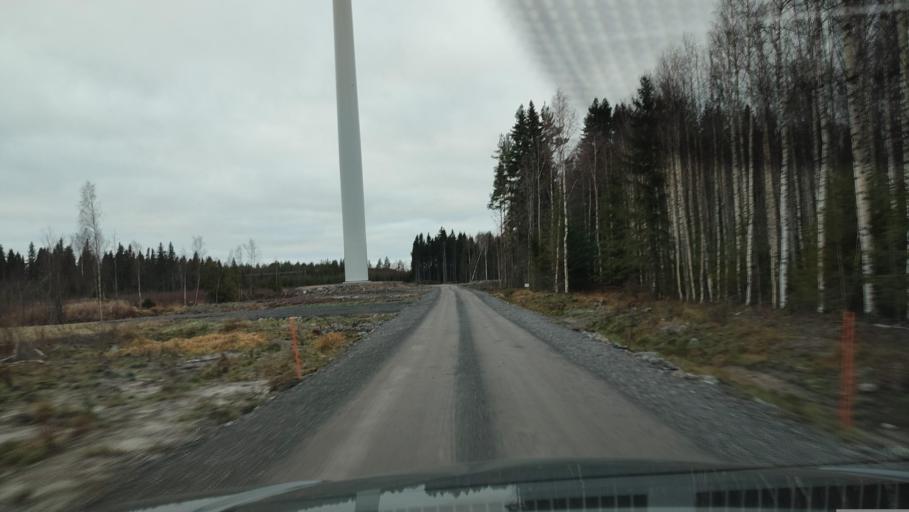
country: FI
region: Southern Ostrobothnia
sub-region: Suupohja
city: Karijoki
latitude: 62.2192
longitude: 21.5997
